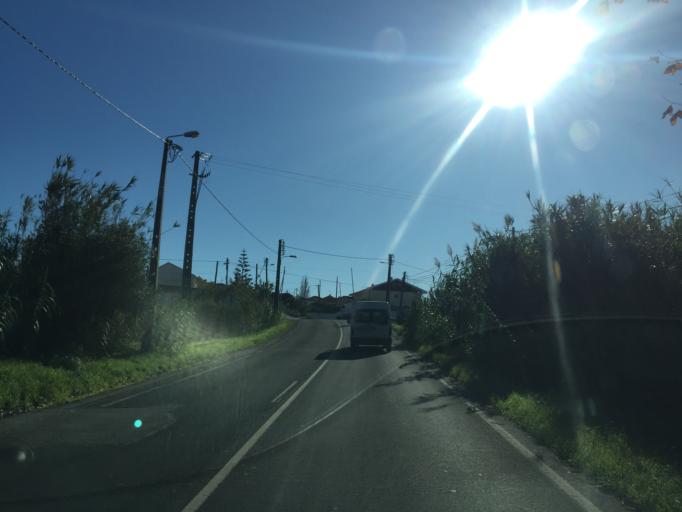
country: PT
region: Lisbon
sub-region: Sintra
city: Almargem
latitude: 38.8277
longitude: -9.3016
